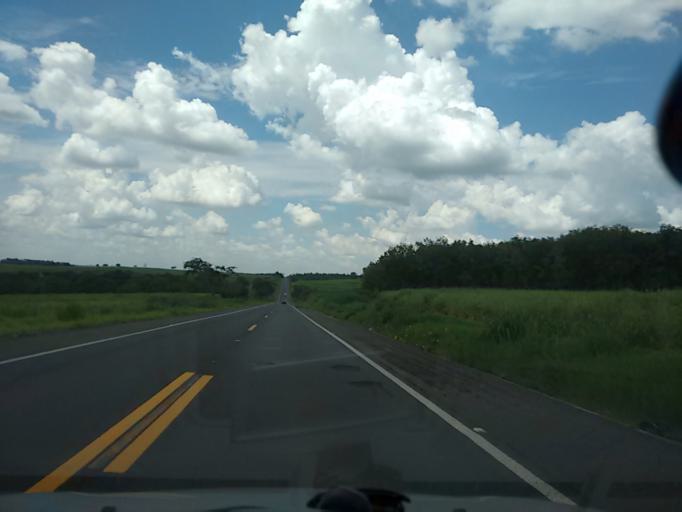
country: BR
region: Sao Paulo
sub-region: Osvaldo Cruz
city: Osvaldo Cruz
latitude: -21.8626
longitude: -50.8477
